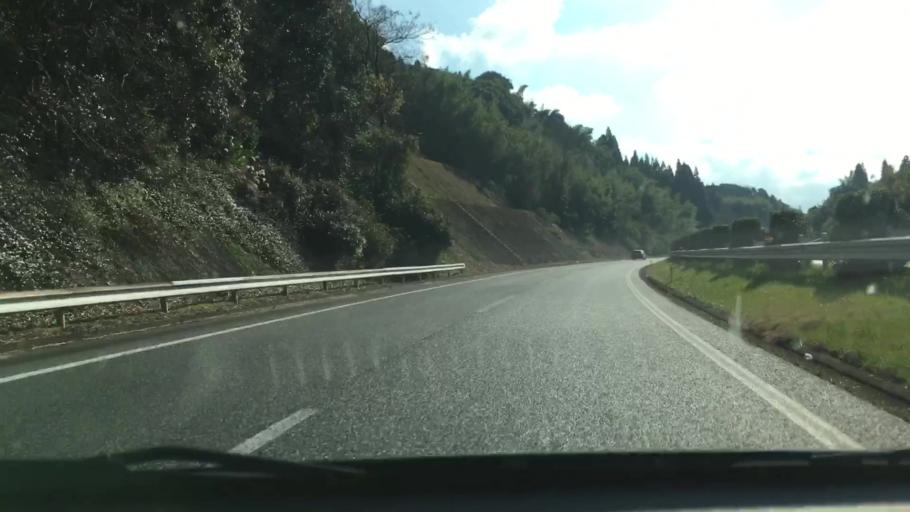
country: JP
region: Kumamoto
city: Matsubase
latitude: 32.6103
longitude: 130.7247
